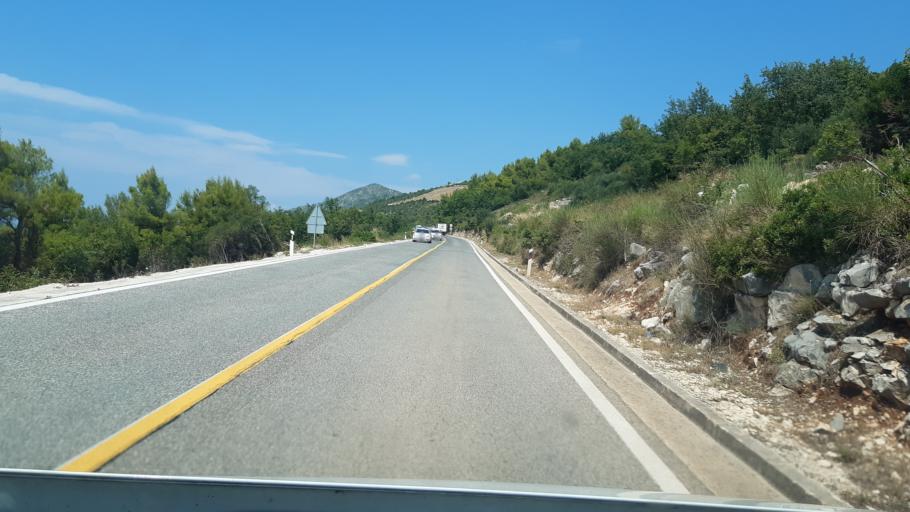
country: HR
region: Dubrovacko-Neretvanska
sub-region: Grad Dubrovnik
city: Opuzen
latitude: 42.9541
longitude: 17.5289
